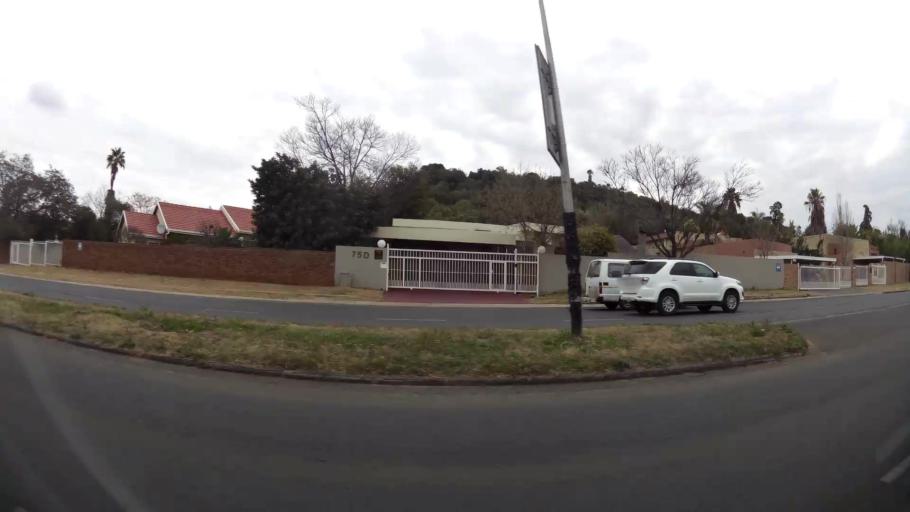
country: ZA
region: Orange Free State
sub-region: Mangaung Metropolitan Municipality
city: Bloemfontein
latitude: -29.0903
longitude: 26.2040
